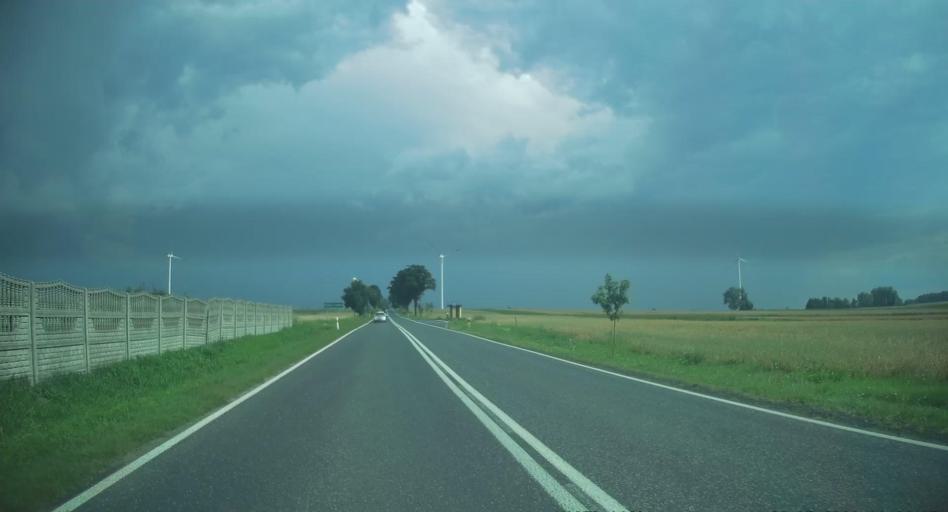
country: PL
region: Lodz Voivodeship
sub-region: Powiat skierniewicki
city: Gluchow
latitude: 51.7979
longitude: 20.0277
